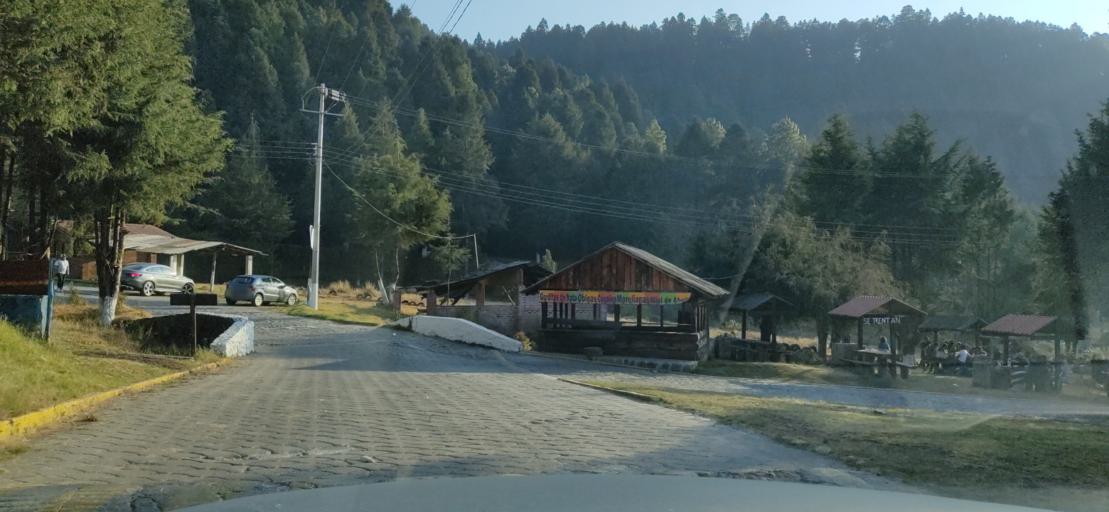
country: MX
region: Mexico
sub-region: Ocoyoacac
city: San Jeronimo Acazulco
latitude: 19.2417
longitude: -99.3773
